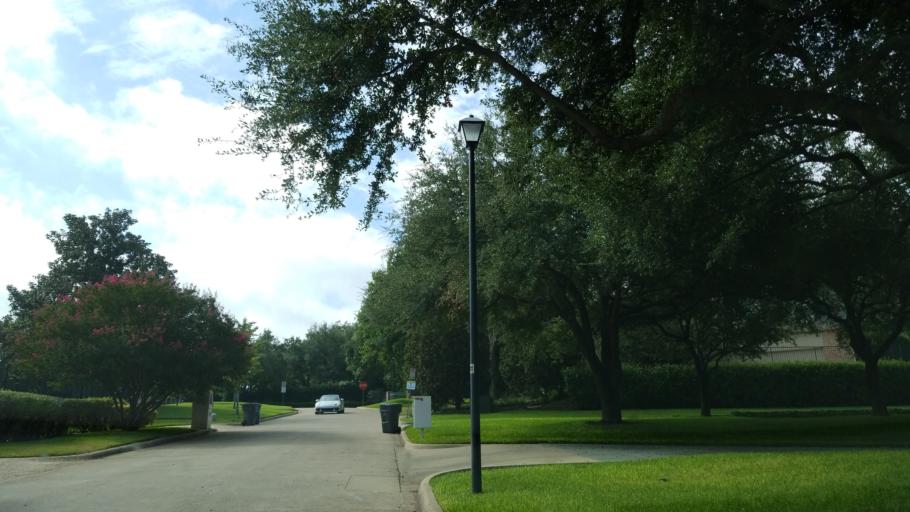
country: US
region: Texas
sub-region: Dallas County
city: Addison
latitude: 32.9446
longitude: -96.7999
